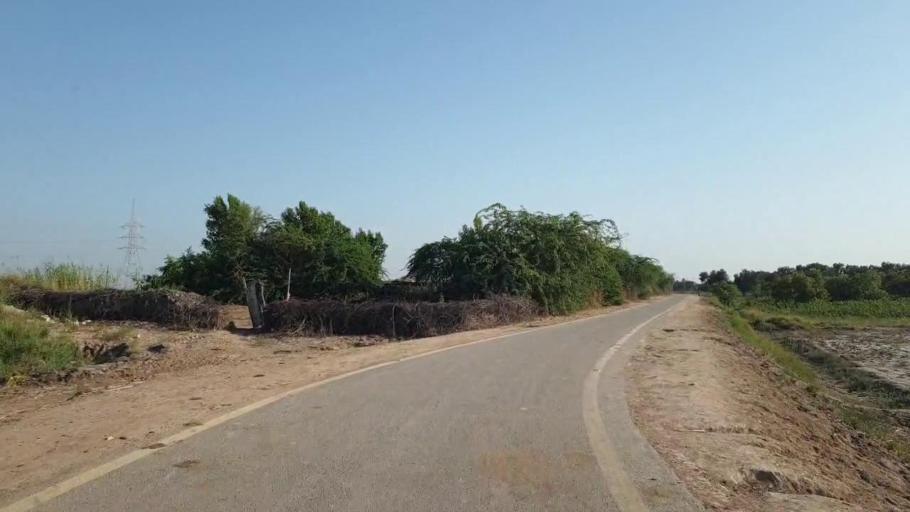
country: PK
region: Sindh
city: Hyderabad
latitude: 25.3377
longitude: 68.4218
